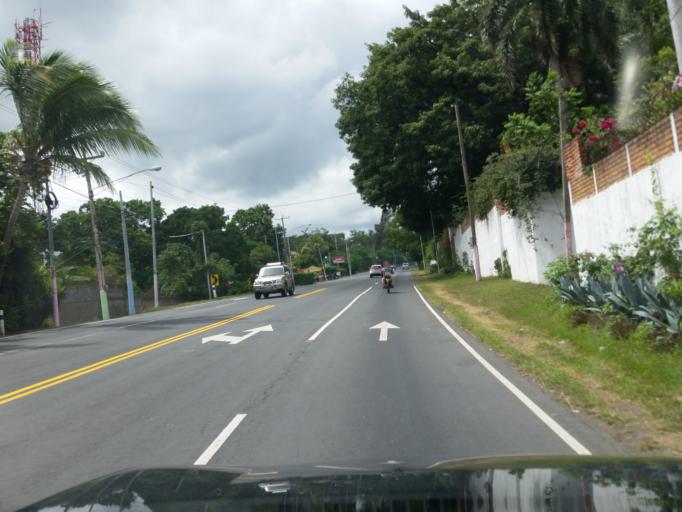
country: NI
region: Managua
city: El Crucero
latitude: 12.0642
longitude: -86.3203
